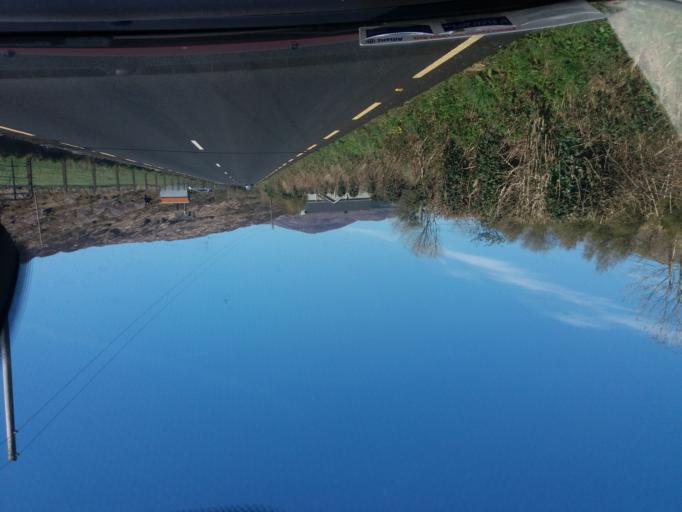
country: IE
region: Munster
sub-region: Ciarrai
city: Cill Airne
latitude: 51.9303
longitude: -9.3833
